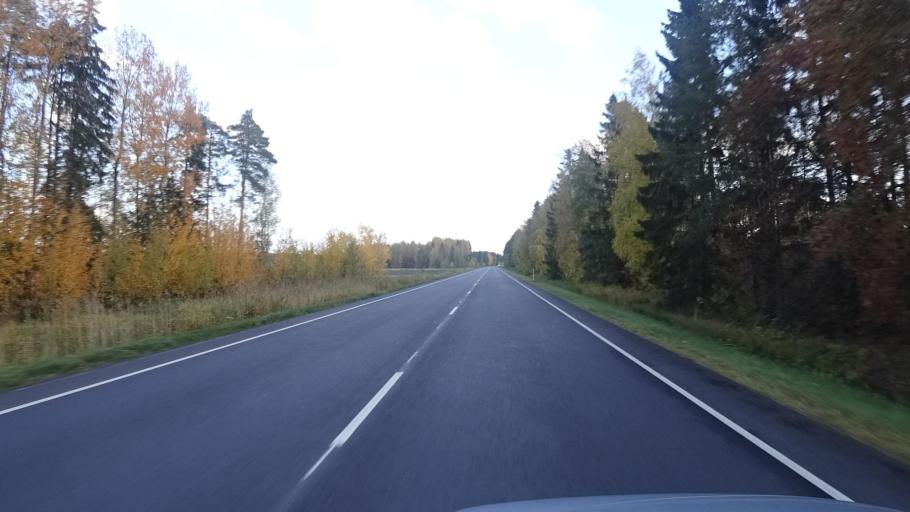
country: FI
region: Satakunta
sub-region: Rauma
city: Koeylioe
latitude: 61.0864
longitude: 22.2585
